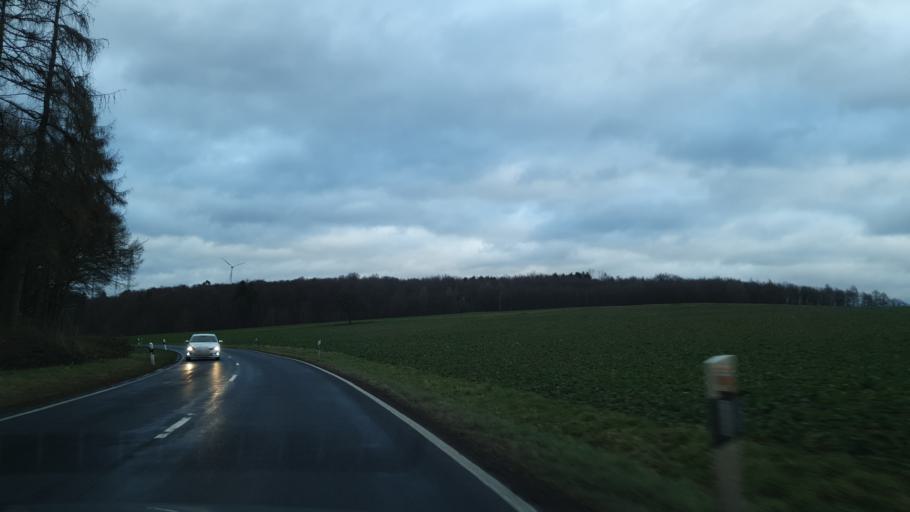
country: DE
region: Rheinland-Pfalz
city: Hirschberg
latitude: 50.3859
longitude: 7.9272
